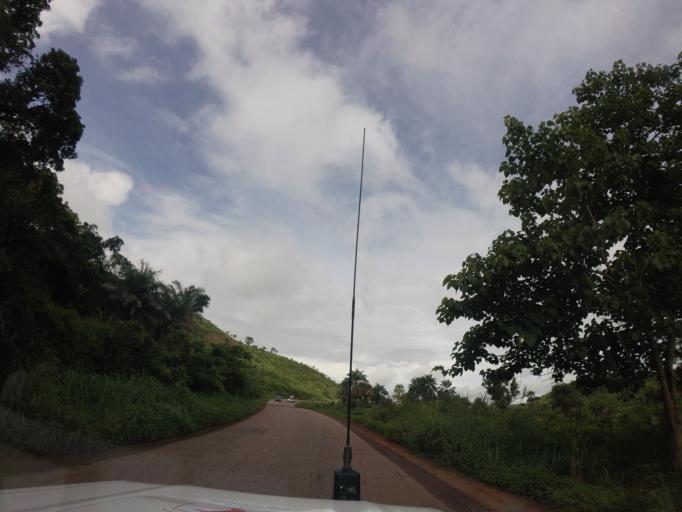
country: GN
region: Kindia
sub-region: Coyah
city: Coyah
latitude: 9.8274
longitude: -13.2551
